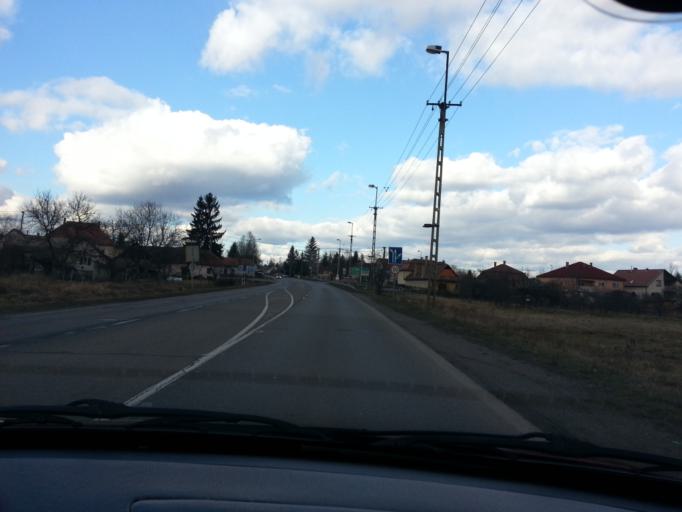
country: HU
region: Nograd
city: Batonyterenye
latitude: 48.0050
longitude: 19.8244
